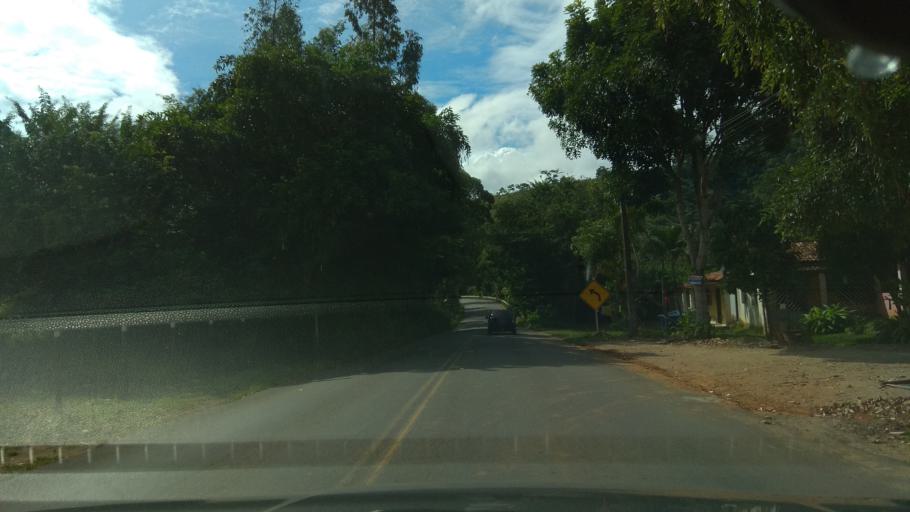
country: BR
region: Bahia
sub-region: Ubaira
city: Ubaira
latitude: -13.2717
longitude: -39.6330
